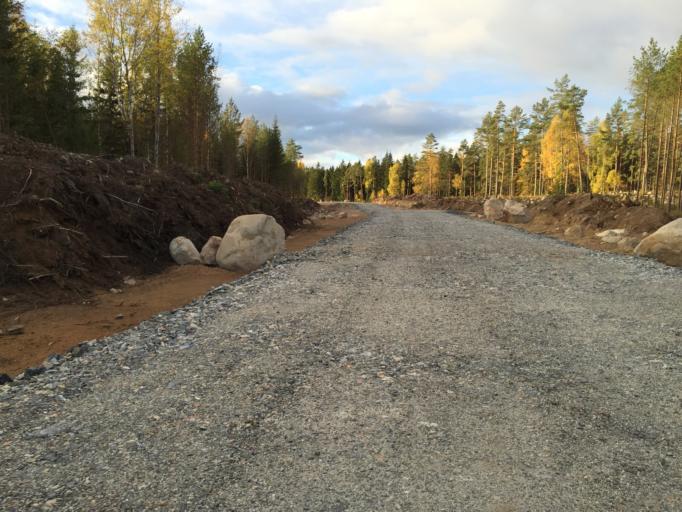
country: SE
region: Vaestmanland
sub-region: Hallstahammars Kommun
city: Hallstahammar
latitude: 59.6352
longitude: 16.2002
